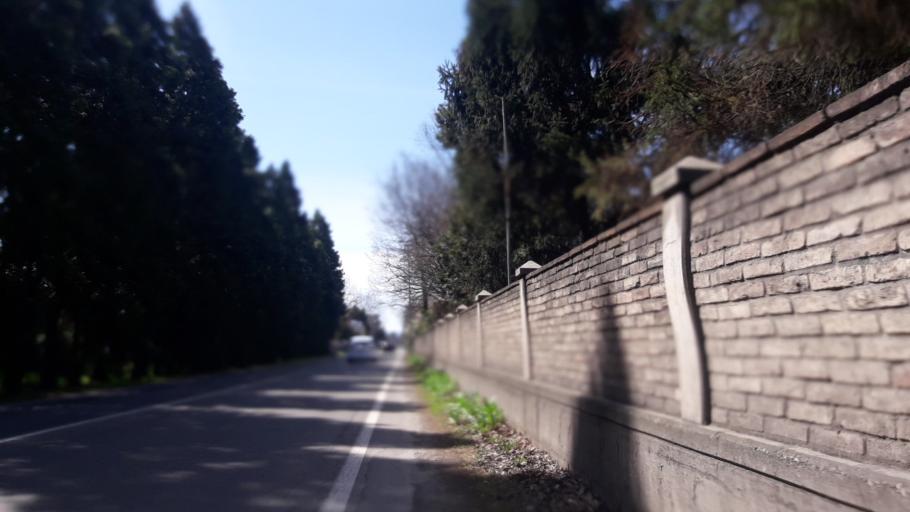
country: IT
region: Emilia-Romagna
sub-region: Provincia di Reggio Emilia
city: Reggio nell'Emilia
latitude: 44.6726
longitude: 10.6094
